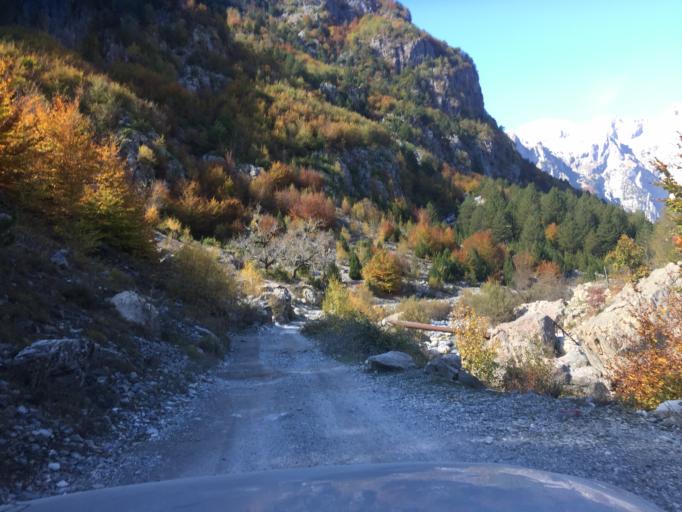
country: AL
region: Shkoder
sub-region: Rrethi i Shkodres
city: Nicaj-Shale
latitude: 42.3856
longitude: 19.7808
